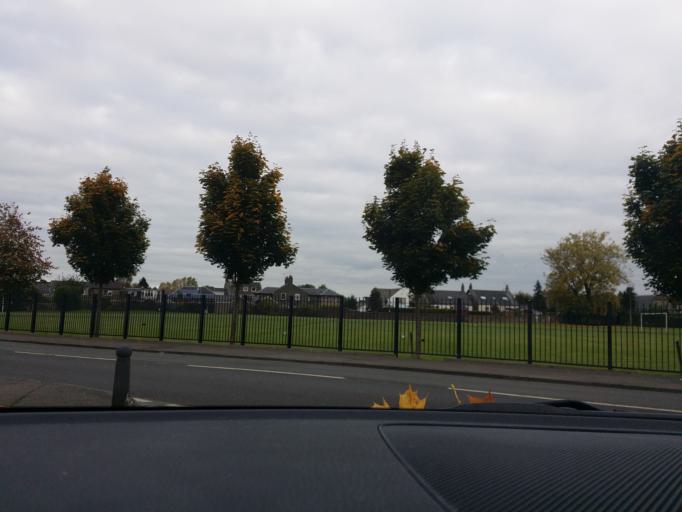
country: GB
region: Scotland
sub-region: Stirling
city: Stirling
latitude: 56.1038
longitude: -3.9479
